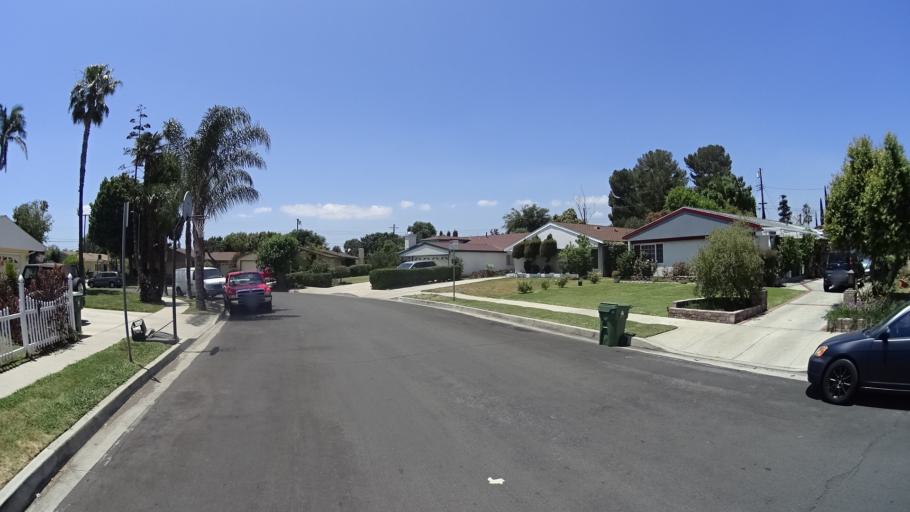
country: US
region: California
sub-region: Los Angeles County
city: Van Nuys
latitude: 34.2239
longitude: -118.4588
